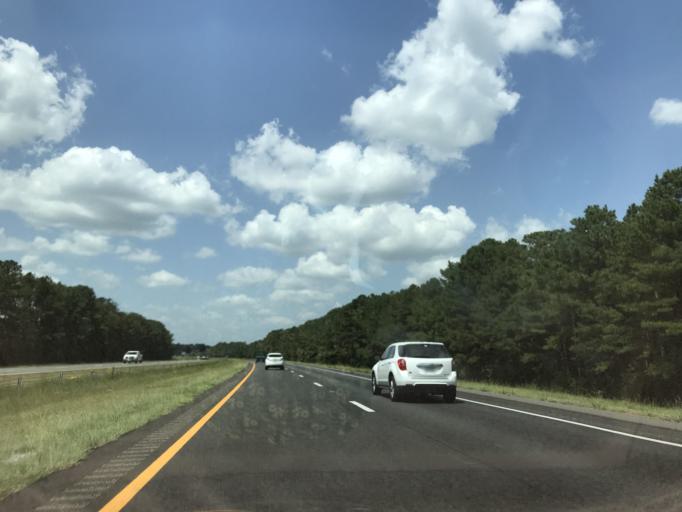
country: US
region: North Carolina
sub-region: Wayne County
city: Mount Olive
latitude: 35.1701
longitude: -78.2507
